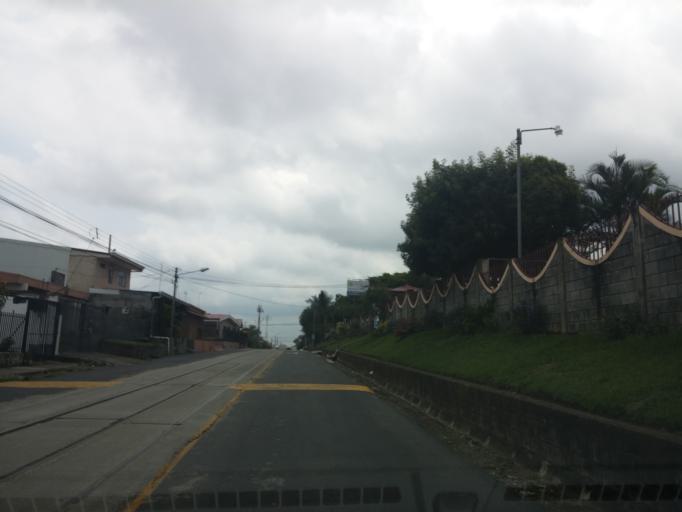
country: CR
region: Heredia
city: Llorente
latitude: 10.0026
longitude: -84.1490
